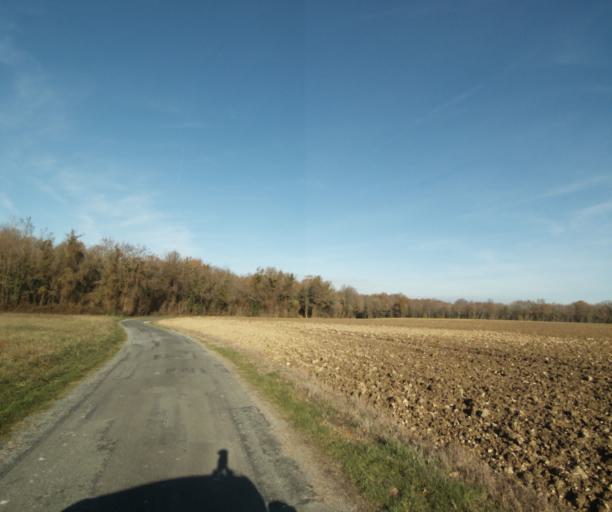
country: FR
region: Poitou-Charentes
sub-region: Departement de la Charente-Maritime
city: Chaniers
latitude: 45.7591
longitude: -0.5101
